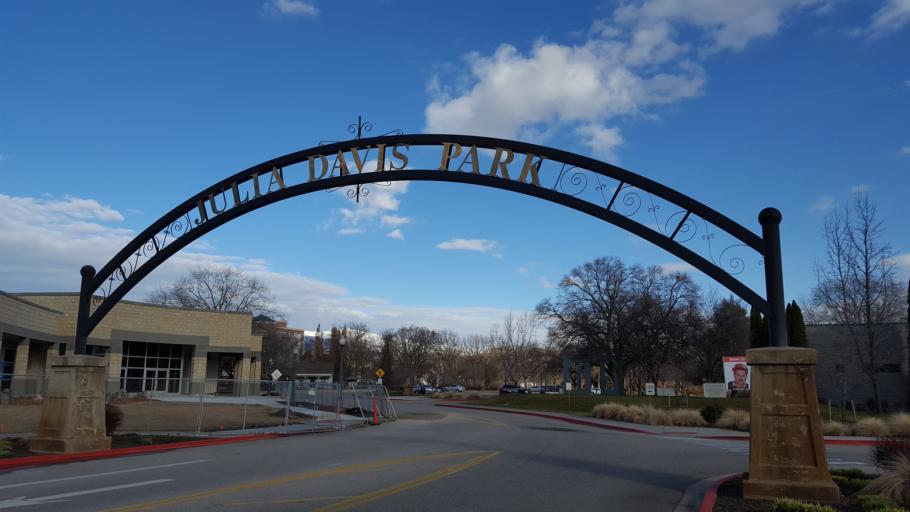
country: US
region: Idaho
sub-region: Ada County
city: Boise
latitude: 43.6086
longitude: -116.2069
